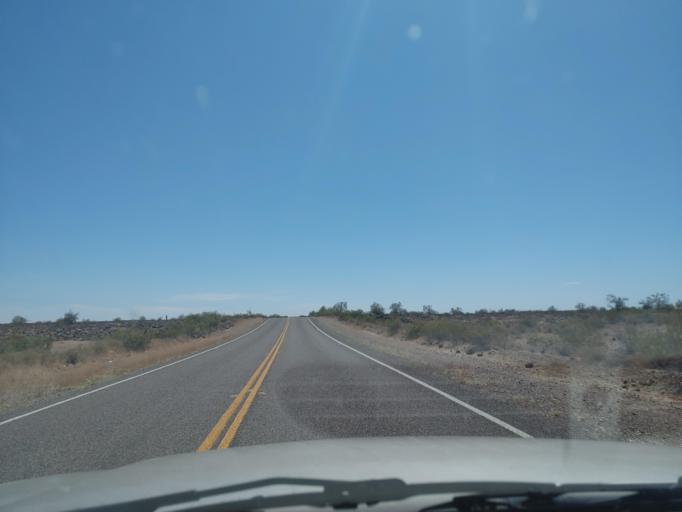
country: US
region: Arizona
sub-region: Maricopa County
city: Gila Bend
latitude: 32.9050
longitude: -113.2627
